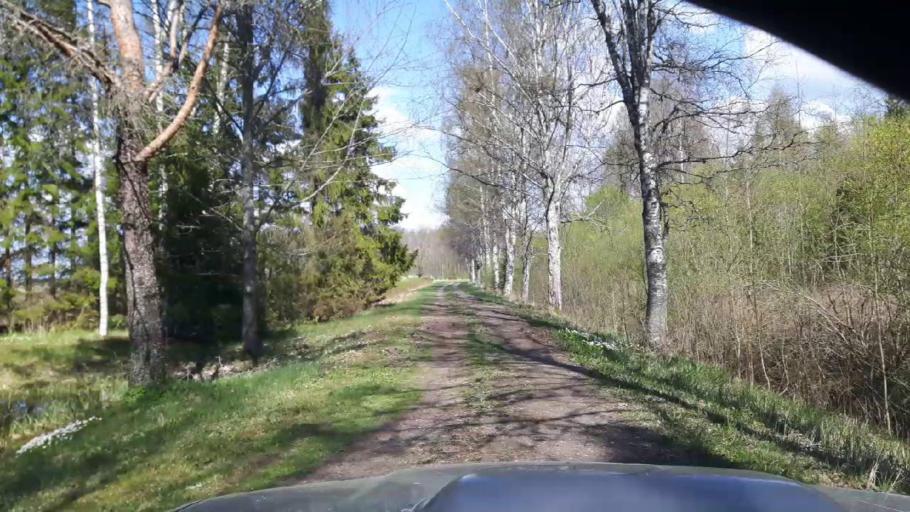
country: EE
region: Paernumaa
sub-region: Tootsi vald
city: Tootsi
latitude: 58.4613
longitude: 24.7967
